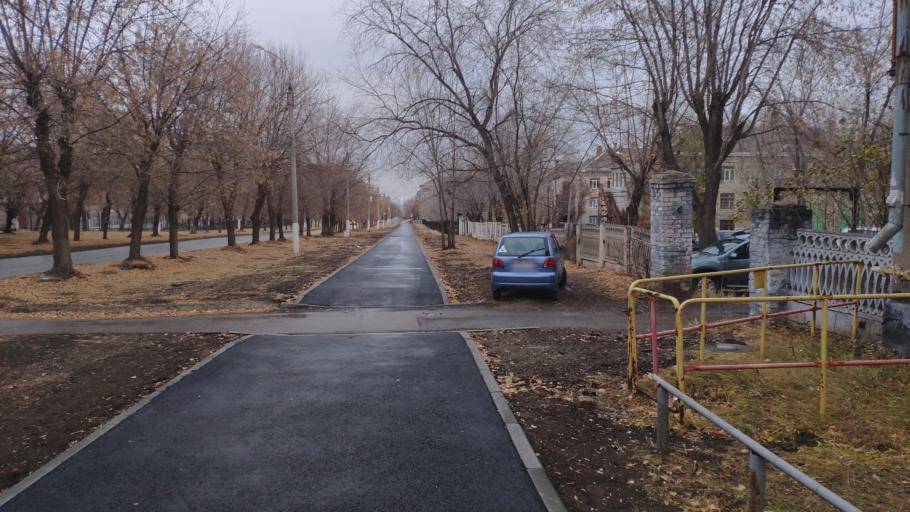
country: RU
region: Chelyabinsk
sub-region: Gorod Magnitogorsk
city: Magnitogorsk
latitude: 53.4044
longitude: 58.9675
